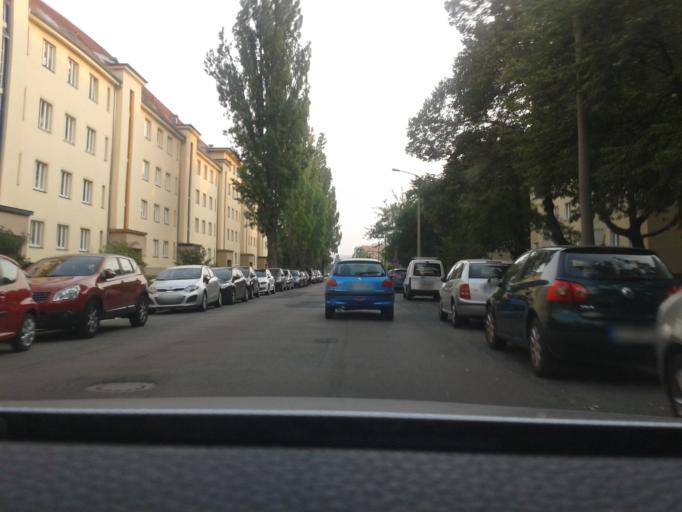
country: DE
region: Saxony
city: Albertstadt
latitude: 51.0336
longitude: 13.8062
